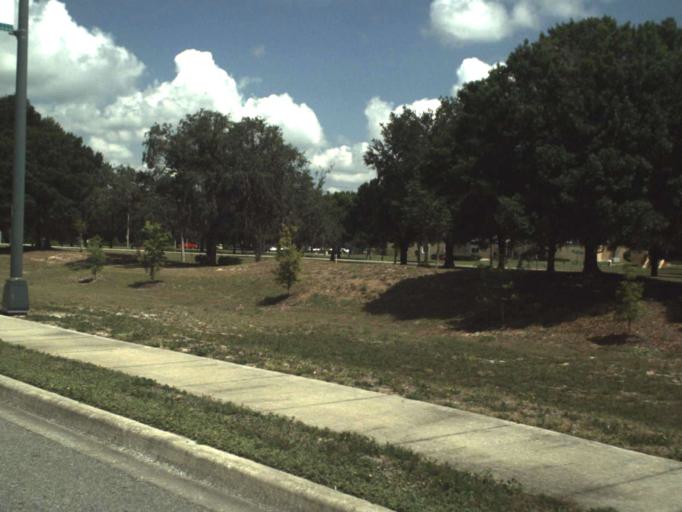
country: US
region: Florida
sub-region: Lake County
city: Silver Lake
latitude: 28.8263
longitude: -81.7970
